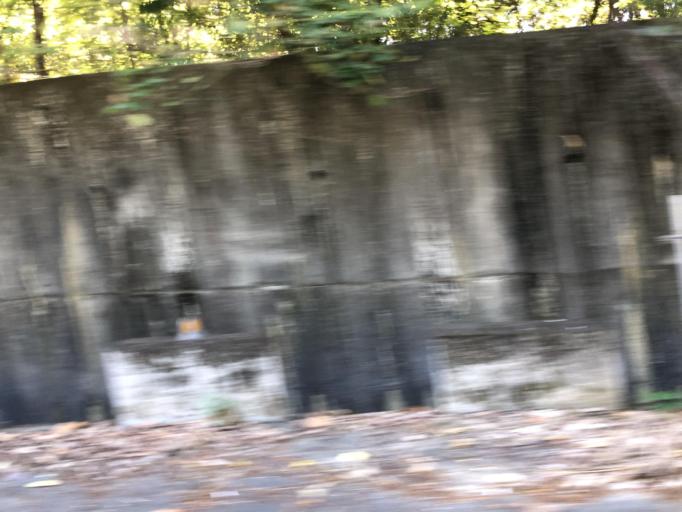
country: TW
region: Taiwan
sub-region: Tainan
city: Tainan
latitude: 23.0345
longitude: 120.3457
